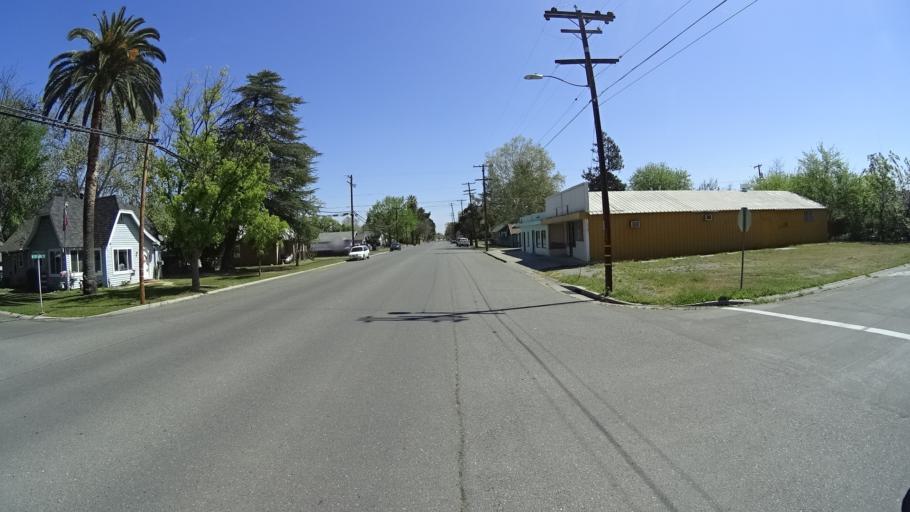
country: US
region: California
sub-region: Glenn County
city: Willows
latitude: 39.5204
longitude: -122.2061
